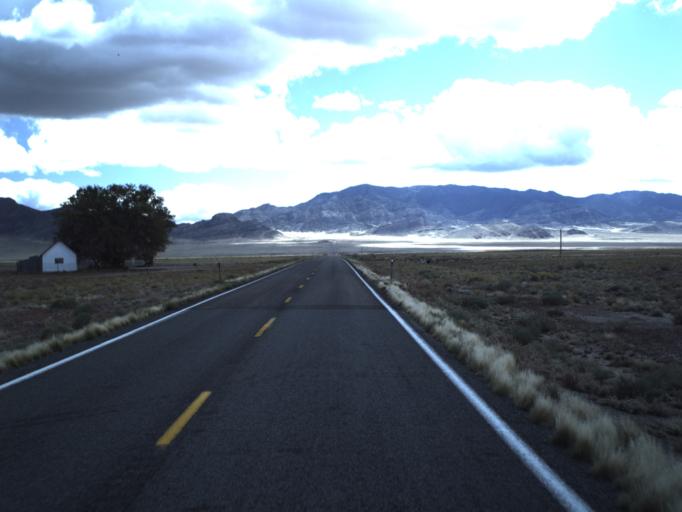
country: US
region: Utah
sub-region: Beaver County
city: Milford
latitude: 38.5369
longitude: -113.6943
